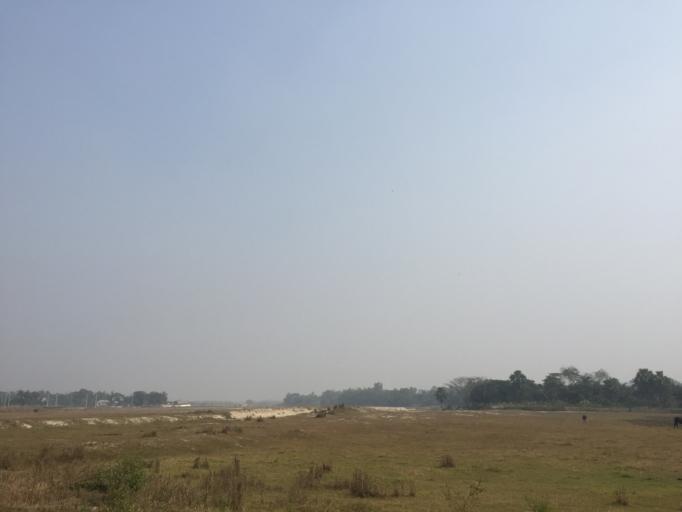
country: BD
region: Dhaka
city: Tungi
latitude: 23.8644
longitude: 90.3163
